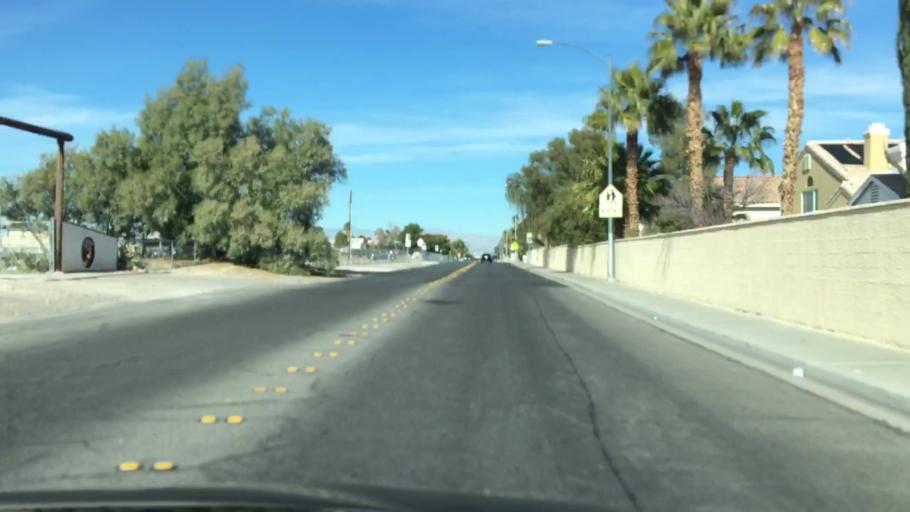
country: US
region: Nevada
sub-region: Clark County
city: Paradise
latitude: 36.0521
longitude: -115.1498
